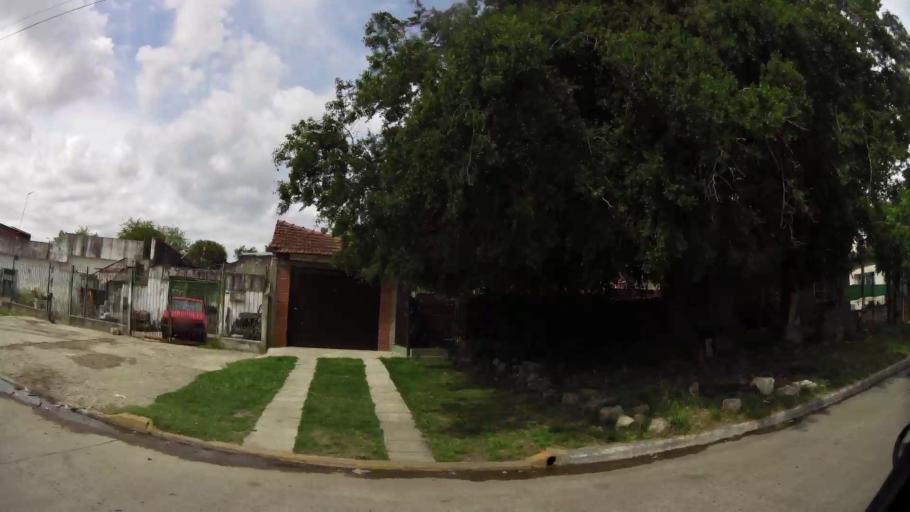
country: AR
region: Buenos Aires
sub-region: Partido de Quilmes
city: Quilmes
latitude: -34.7564
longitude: -58.2506
